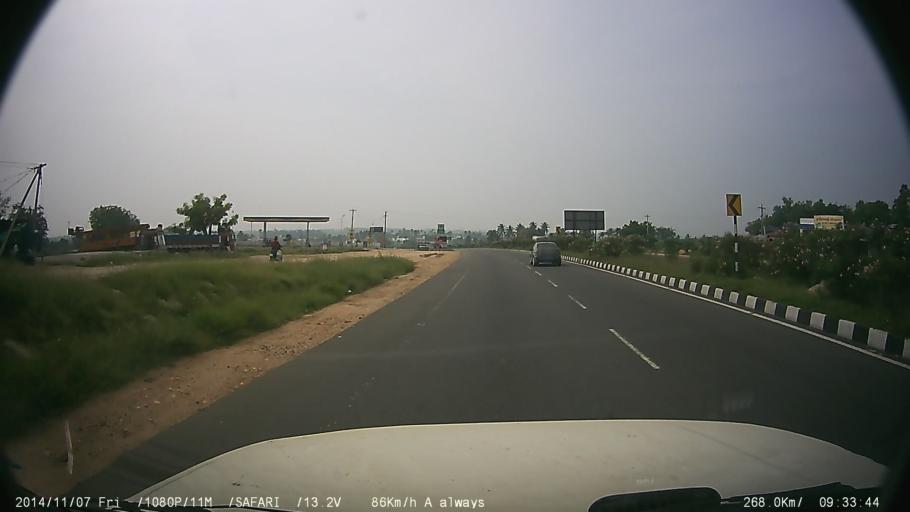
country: IN
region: Tamil Nadu
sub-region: Erode
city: Bhavani
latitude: 11.3969
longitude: 77.6515
